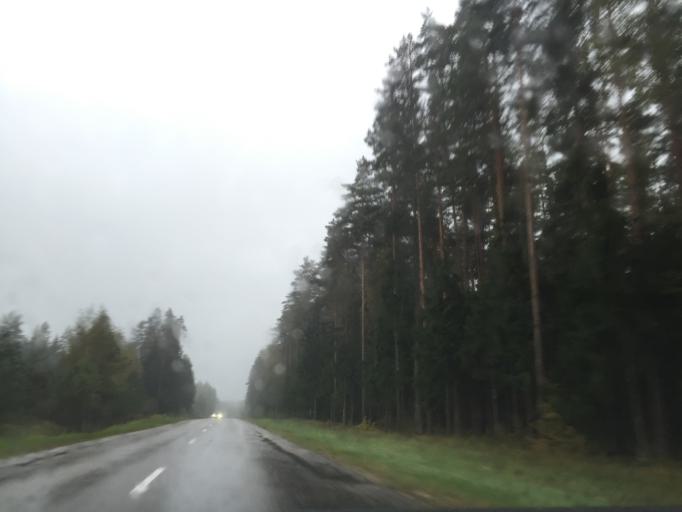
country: LV
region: Ropazu
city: Ropazi
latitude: 57.0183
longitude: 24.6830
